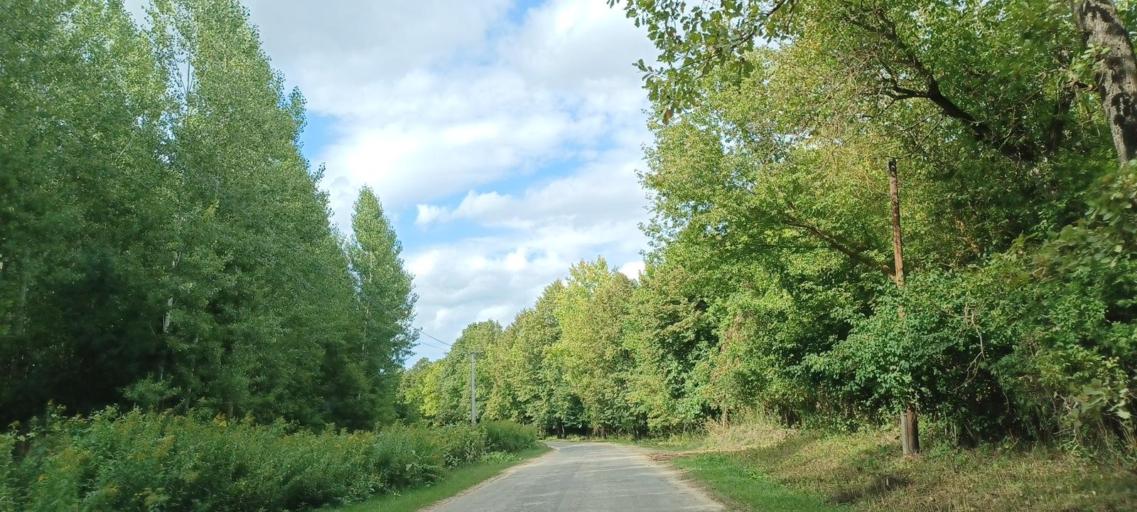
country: HU
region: Tolna
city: Szentgalpuszta
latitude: 46.3456
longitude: 18.6214
